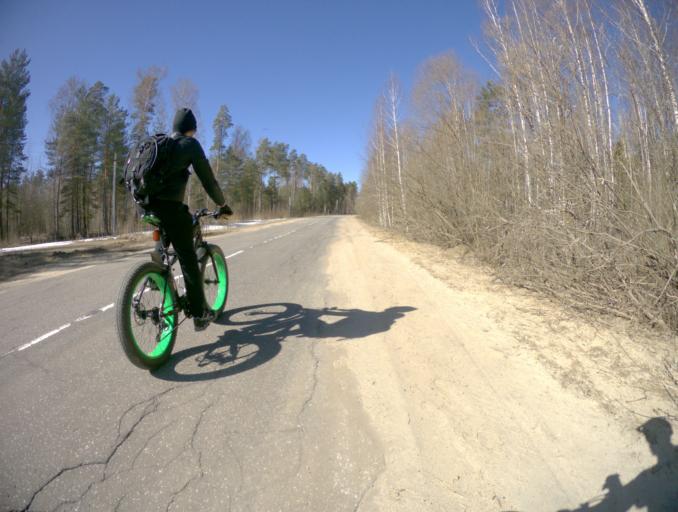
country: RU
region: Vladimir
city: Kameshkovo
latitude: 56.3482
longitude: 40.8462
